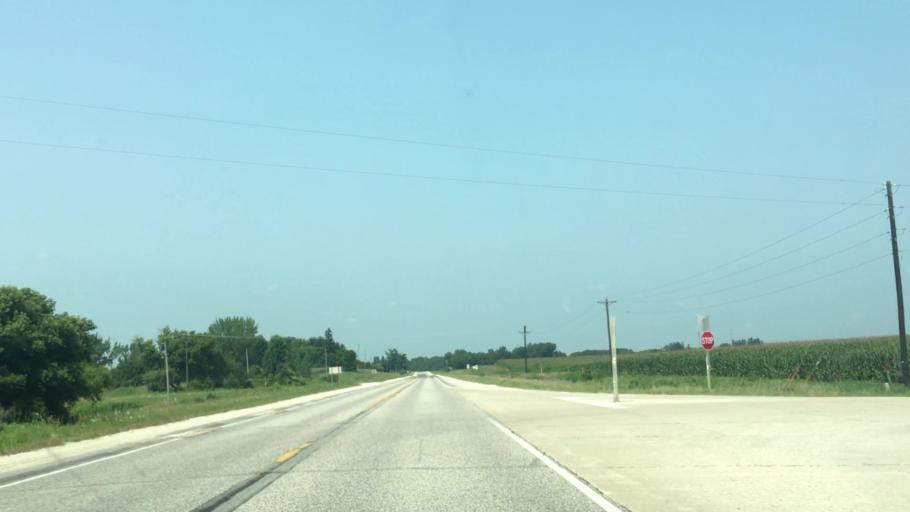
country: US
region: Iowa
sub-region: Fayette County
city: Fayette
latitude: 42.8179
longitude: -91.8051
